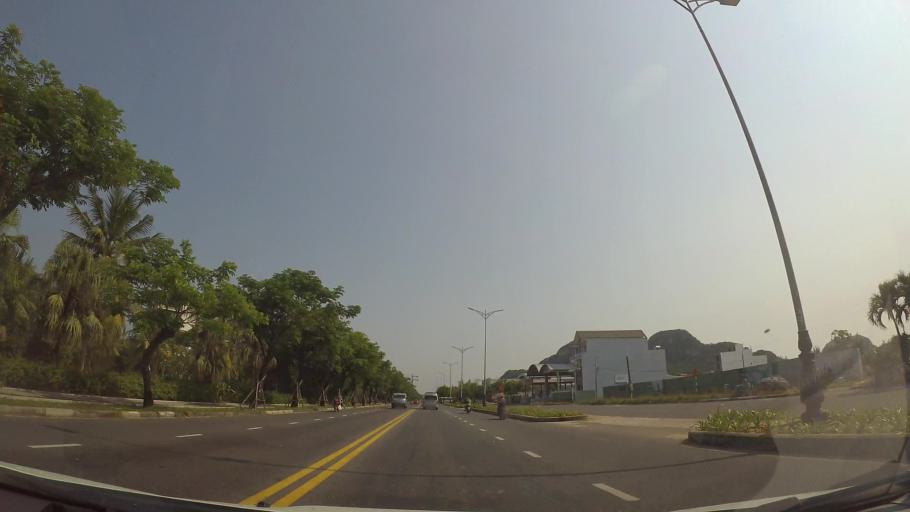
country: VN
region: Da Nang
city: Ngu Hanh Son
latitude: 16.0109
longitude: 108.2630
